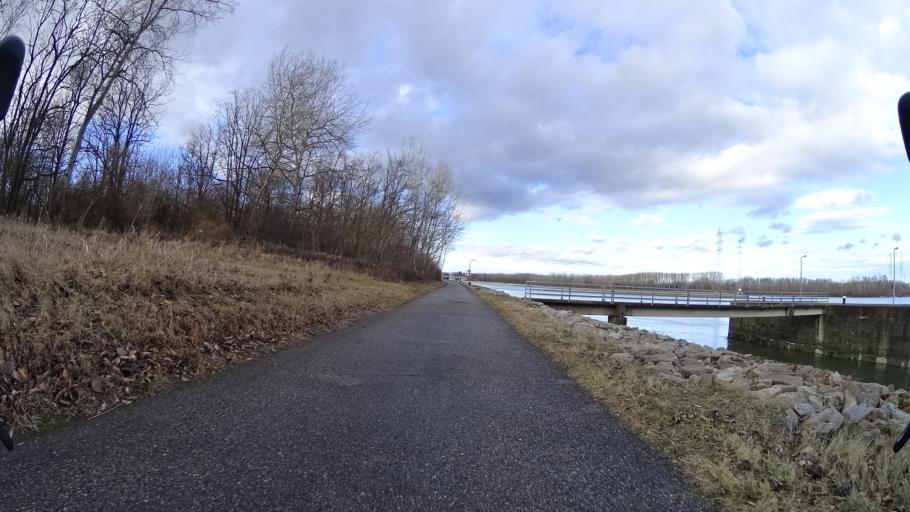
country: AT
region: Lower Austria
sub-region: Politischer Bezirk Tulln
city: Kirchberg am Wagram
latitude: 48.3693
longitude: 15.8714
